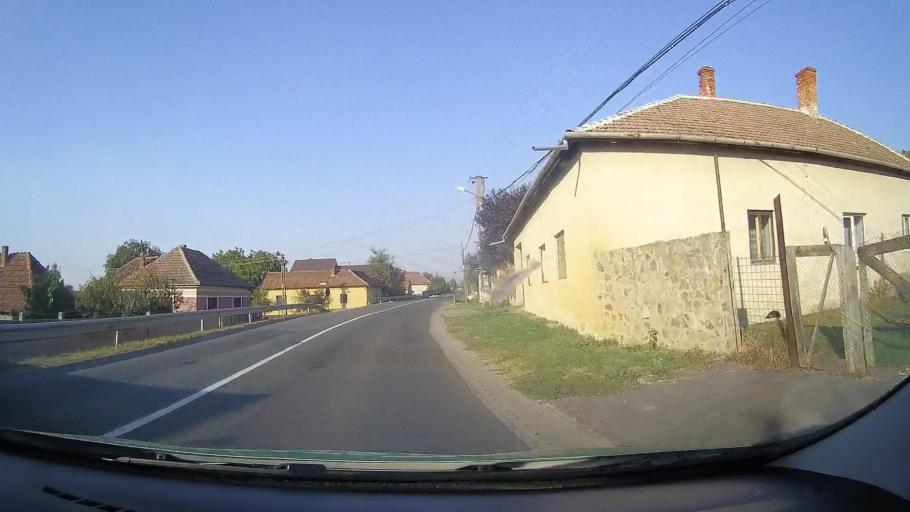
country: RO
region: Arad
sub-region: Comuna Ghioroc
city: Cuvin
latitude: 46.1630
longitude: 21.5917
